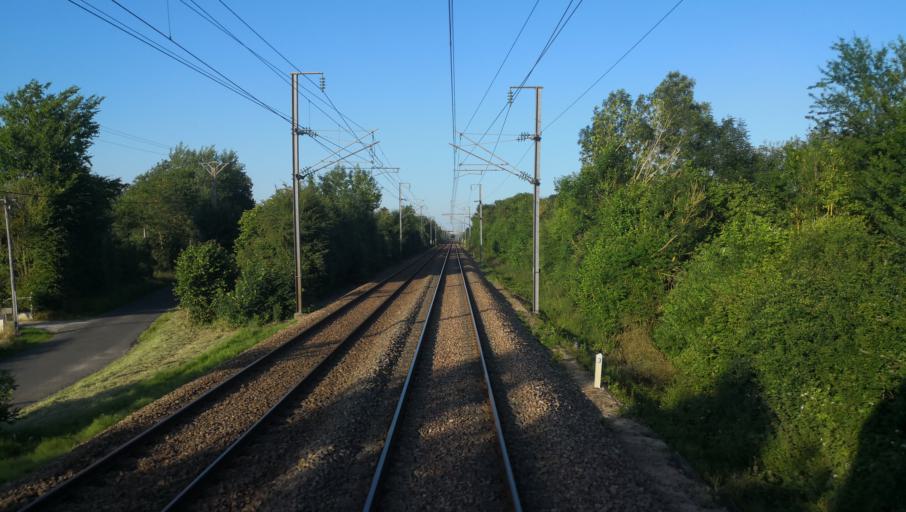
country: FR
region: Haute-Normandie
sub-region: Departement de l'Eure
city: Thiberville
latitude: 49.0760
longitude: 0.4657
